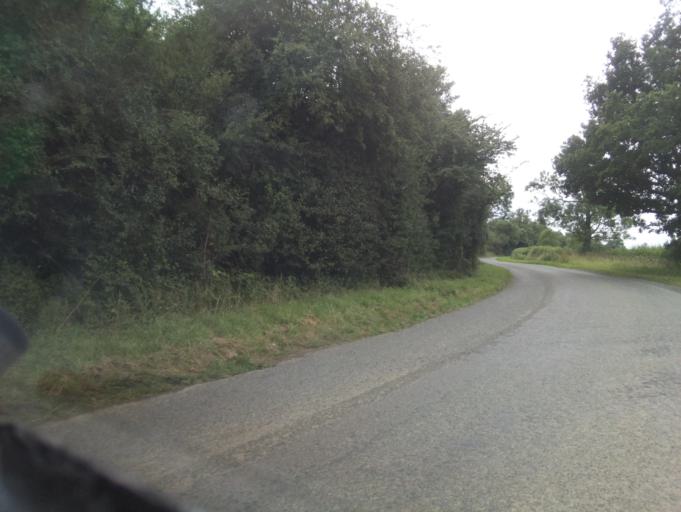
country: GB
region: England
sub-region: District of Rutland
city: Seaton
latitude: 52.5236
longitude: -0.6276
